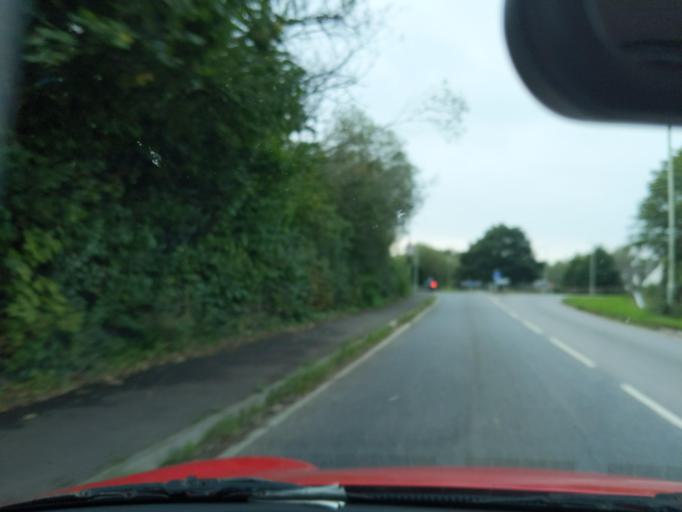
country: GB
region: England
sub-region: Devon
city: Okehampton
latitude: 50.8179
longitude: -4.0731
